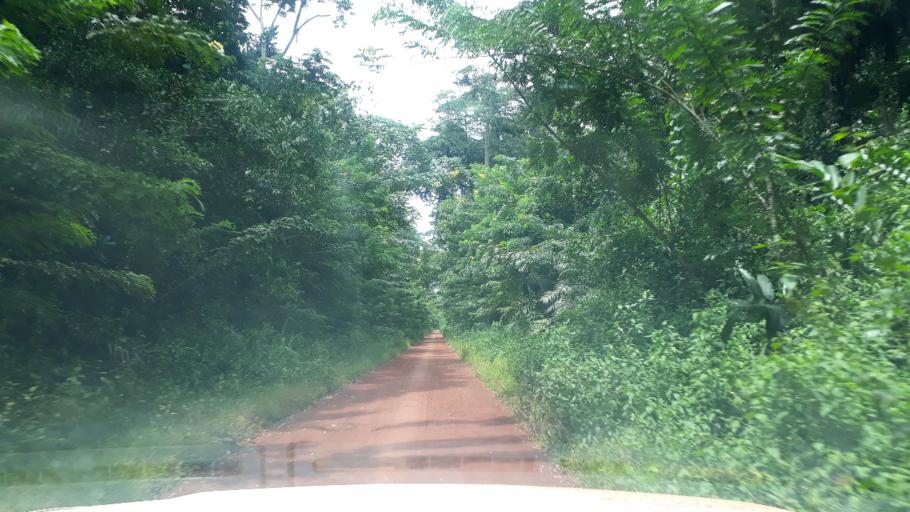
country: CD
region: Eastern Province
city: Aketi
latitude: 2.9268
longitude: 24.0851
